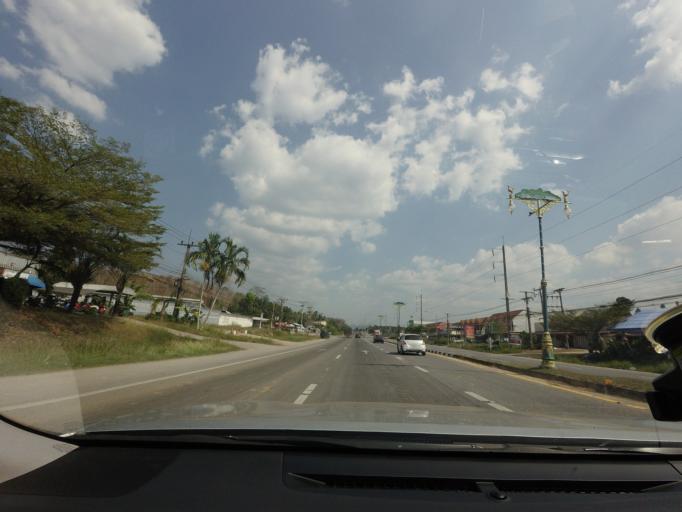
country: TH
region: Phangnga
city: Thap Put
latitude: 8.5133
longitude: 98.6423
